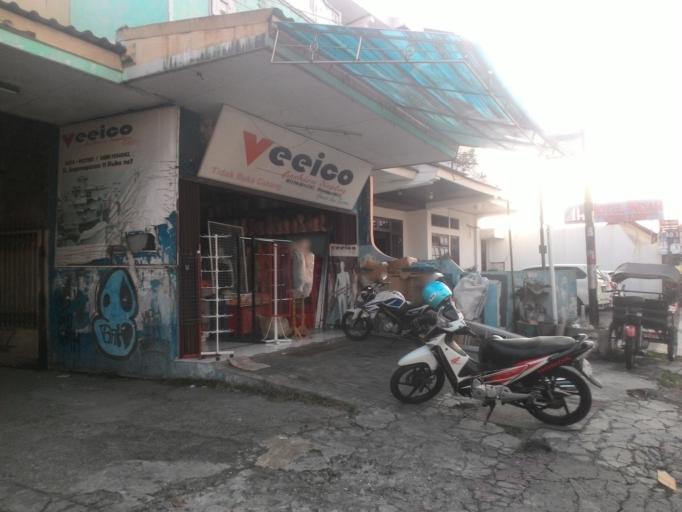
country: ID
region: Daerah Istimewa Yogyakarta
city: Yogyakarta
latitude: -7.7957
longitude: 110.3617
